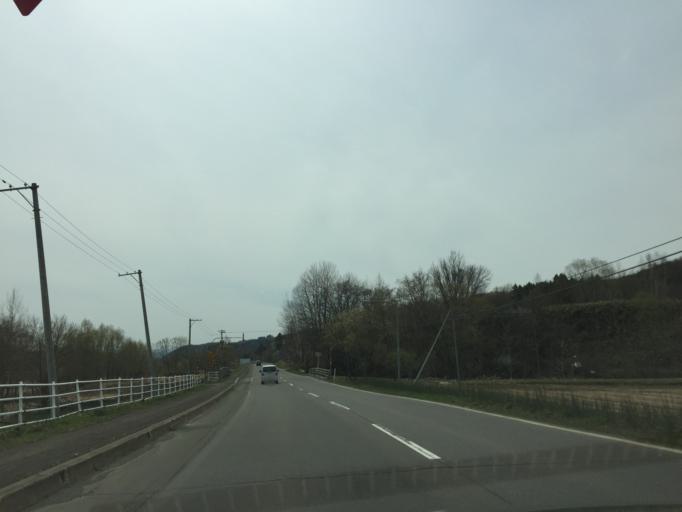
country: JP
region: Hokkaido
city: Ashibetsu
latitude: 43.5908
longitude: 142.1961
